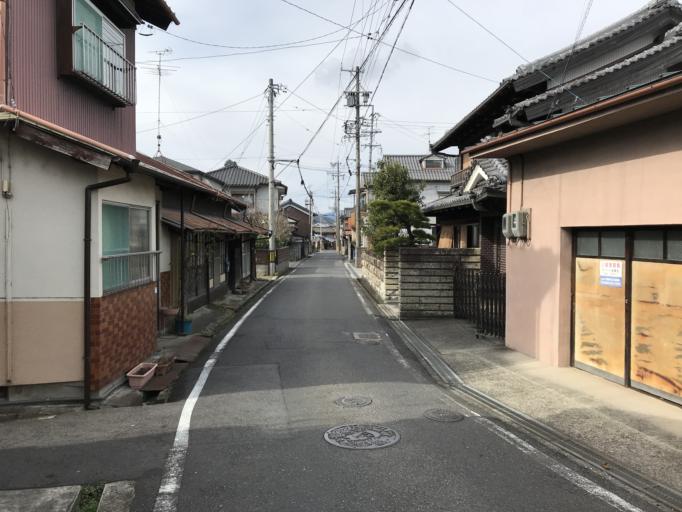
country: JP
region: Mie
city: Ueno-ebisumachi
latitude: 34.7594
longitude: 136.1350
